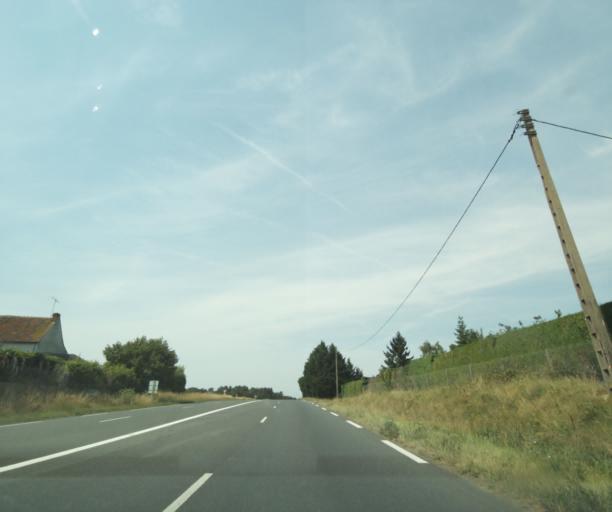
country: FR
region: Centre
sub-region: Departement d'Indre-et-Loire
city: La Celle-Saint-Avant
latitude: 47.0590
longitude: 0.6162
